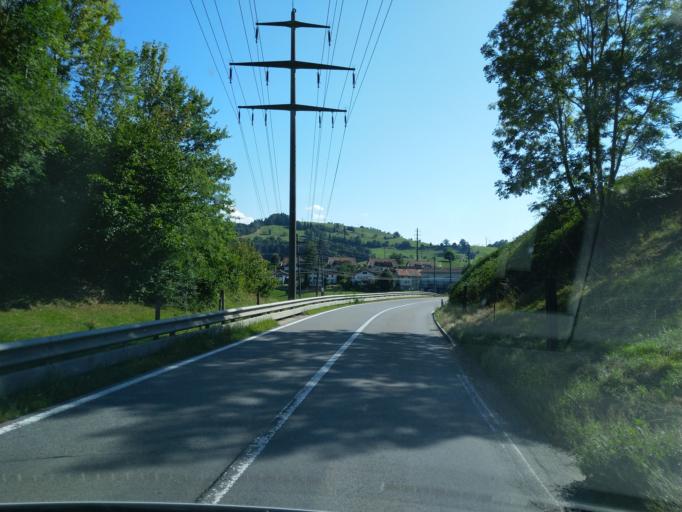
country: CH
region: Lucerne
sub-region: Entlebuch District
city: Werthenstein
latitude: 47.0603
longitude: 8.0945
